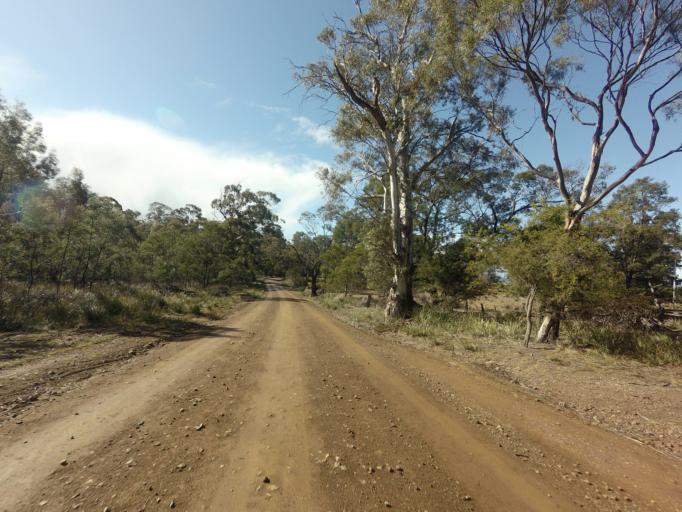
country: AU
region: Tasmania
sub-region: Sorell
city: Sorell
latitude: -42.4052
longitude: 147.9645
